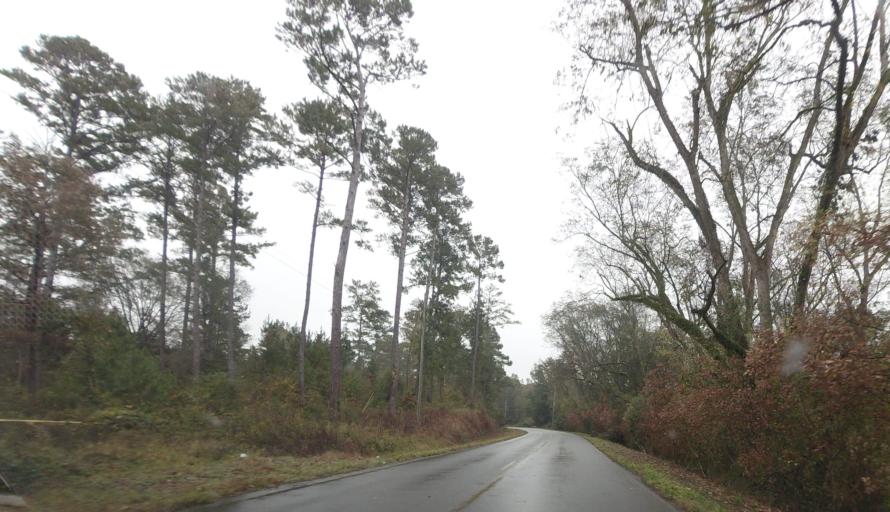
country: US
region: Georgia
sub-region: Peach County
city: Fort Valley
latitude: 32.5360
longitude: -83.9329
